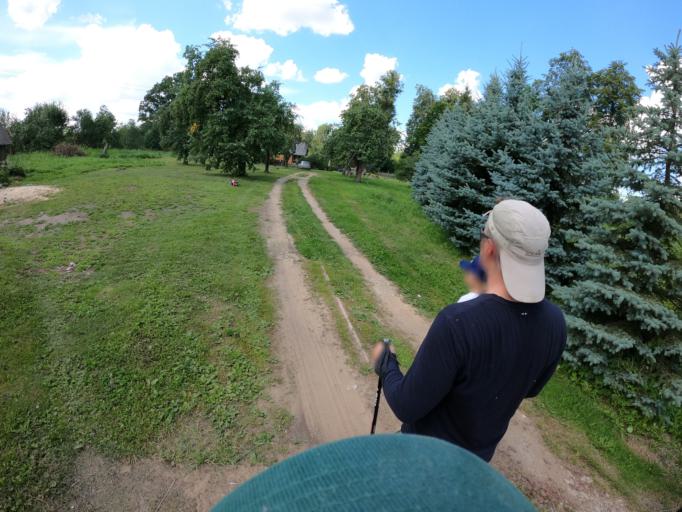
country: LT
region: Alytaus apskritis
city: Druskininkai
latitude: 54.0850
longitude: 24.1643
